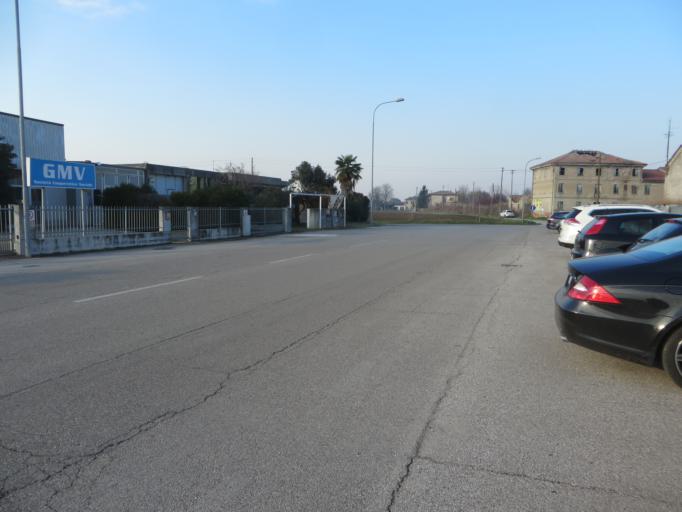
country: IT
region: Veneto
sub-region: Provincia di Verona
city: San Pietro di Morubio
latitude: 45.2312
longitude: 11.2427
